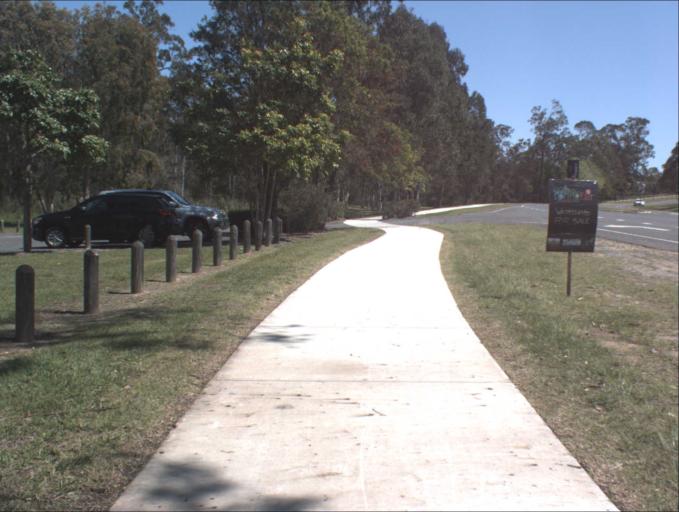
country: AU
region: Queensland
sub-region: Logan
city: North Maclean
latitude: -27.8144
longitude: 152.9641
